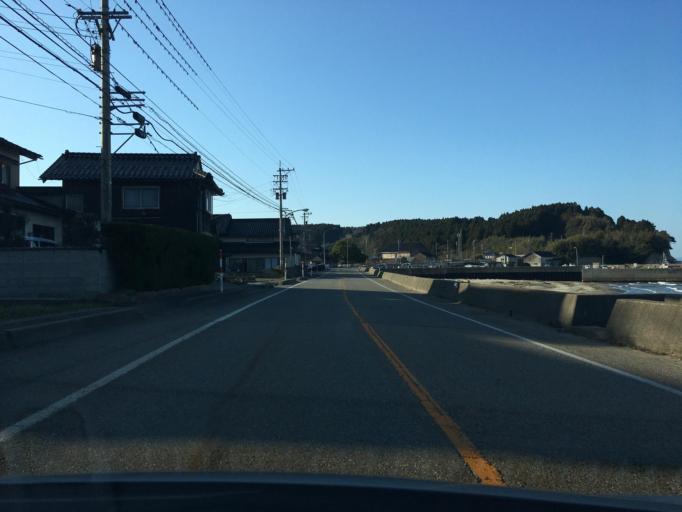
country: JP
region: Ishikawa
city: Nanao
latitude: 36.9757
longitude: 137.0505
